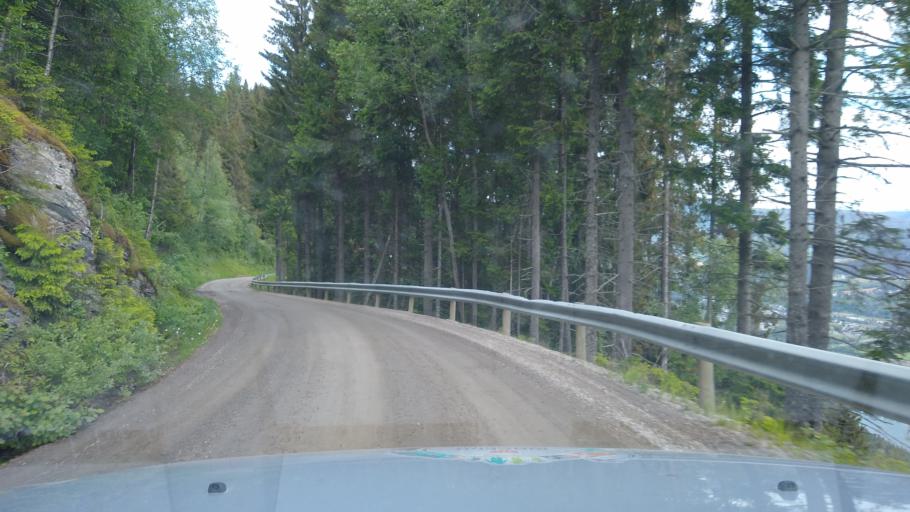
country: NO
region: Oppland
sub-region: Ringebu
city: Ringebu
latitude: 61.5008
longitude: 10.1406
